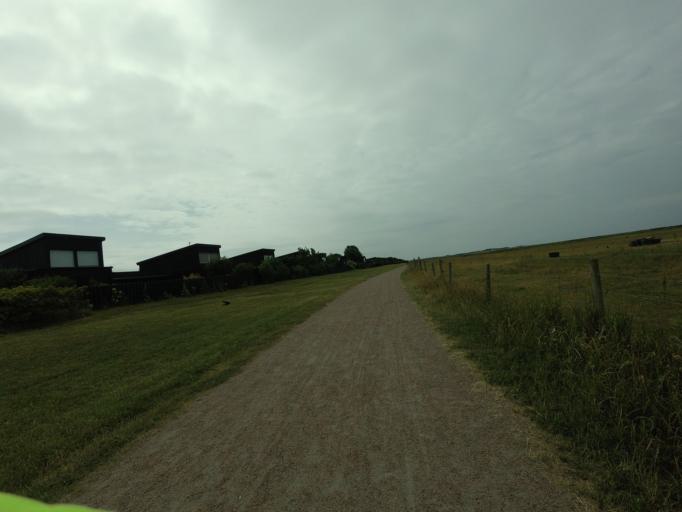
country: SE
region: Skane
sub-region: Malmo
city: Bunkeflostrand
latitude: 55.5531
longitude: 12.9083
